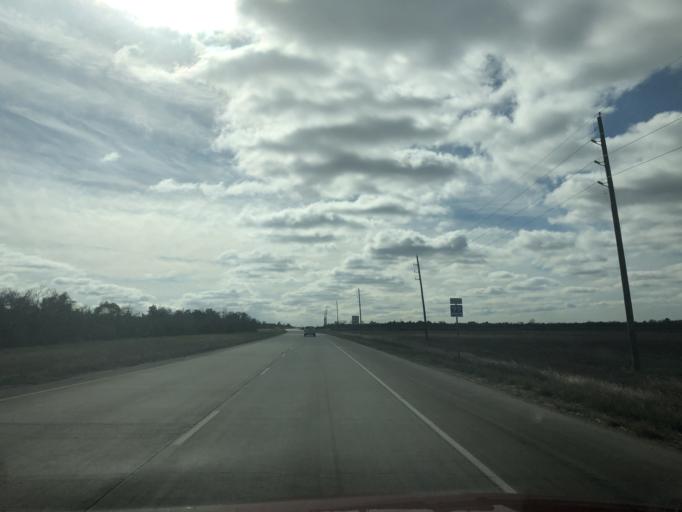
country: US
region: Texas
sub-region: Chambers County
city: Mont Belvieu
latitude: 29.7601
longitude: -94.8737
